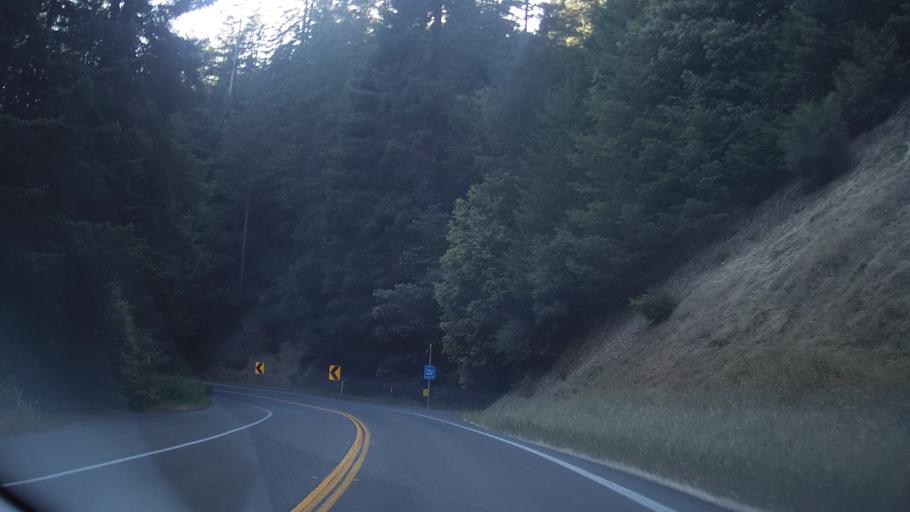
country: US
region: California
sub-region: Mendocino County
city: Brooktrails
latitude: 39.3474
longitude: -123.5244
